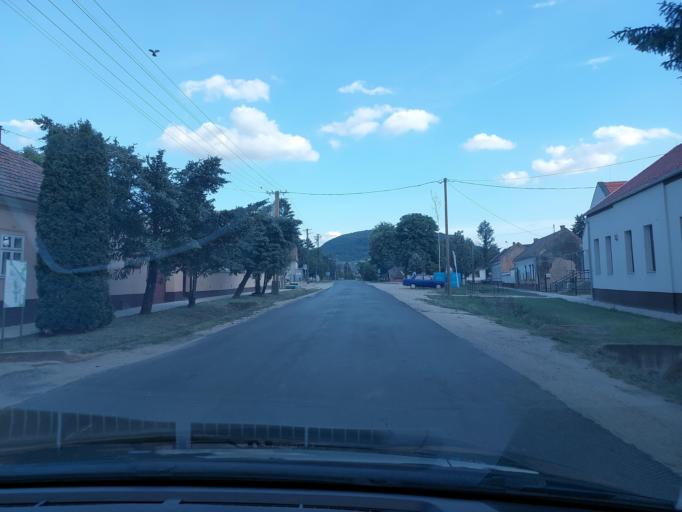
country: HU
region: Veszprem
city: Devecser
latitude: 47.1697
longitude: 17.3600
